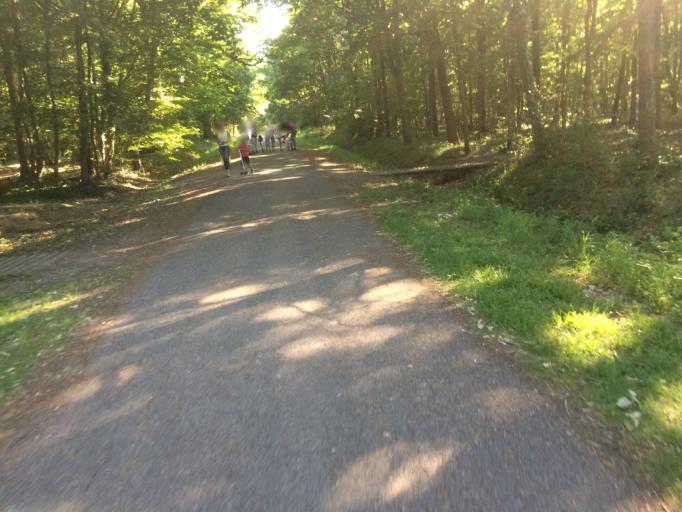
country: FR
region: Ile-de-France
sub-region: Departement du Val-de-Marne
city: Sucy-en-Brie
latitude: 48.7495
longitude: 2.5357
